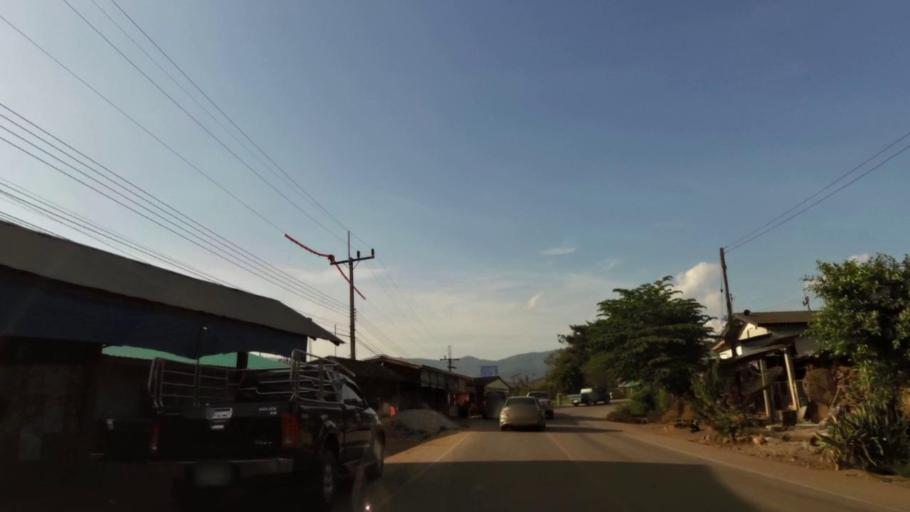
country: TH
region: Chiang Rai
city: Khun Tan
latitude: 19.8677
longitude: 100.3993
